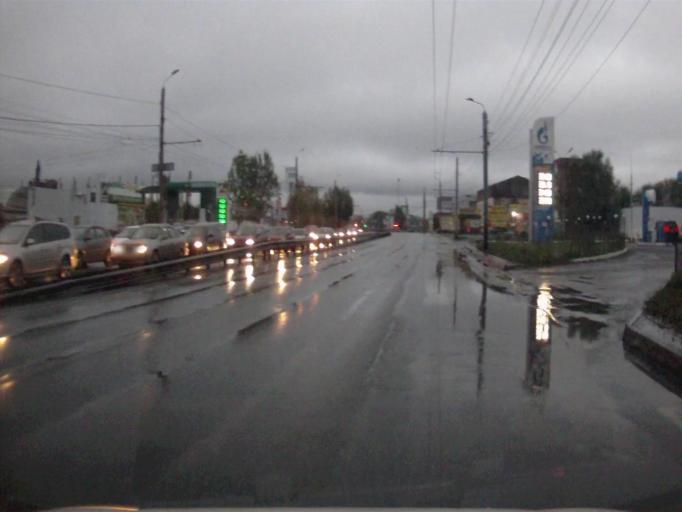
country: RU
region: Chelyabinsk
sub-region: Gorod Chelyabinsk
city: Chelyabinsk
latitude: 55.1400
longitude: 61.4552
